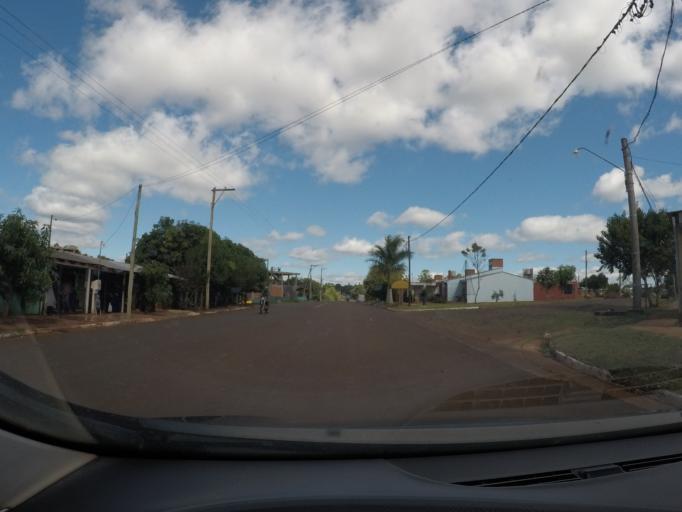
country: AR
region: Misiones
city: Puerto Rico
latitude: -26.8024
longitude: -55.0138
